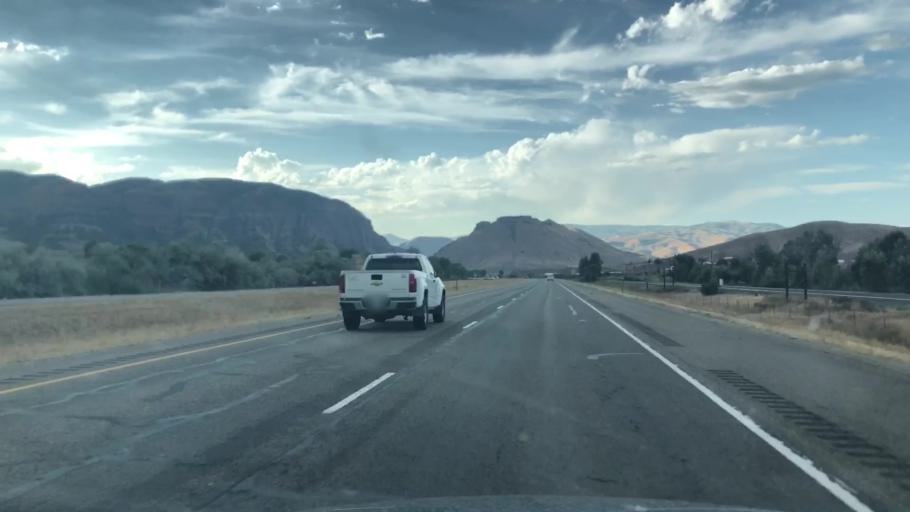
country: US
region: Utah
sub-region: Summit County
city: Coalville
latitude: 41.0221
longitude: -111.4946
